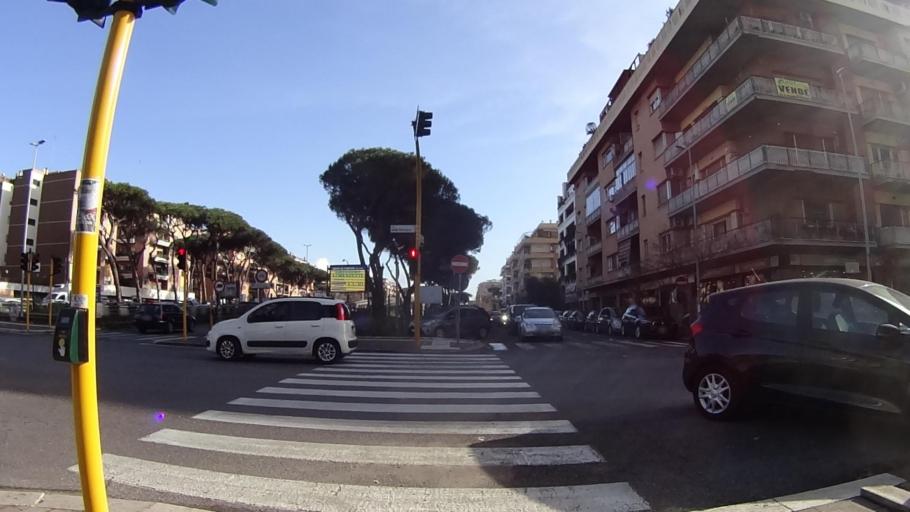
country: IT
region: Latium
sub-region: Citta metropolitana di Roma Capitale
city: Lido di Ostia
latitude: 41.7381
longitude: 12.2783
